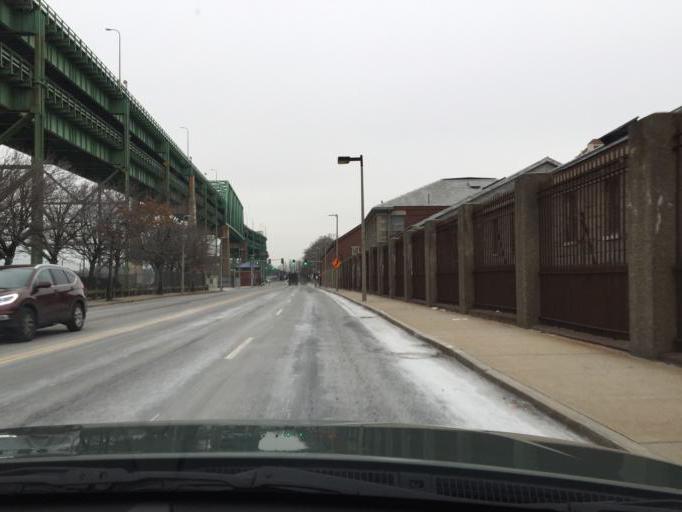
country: US
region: Massachusetts
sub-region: Suffolk County
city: Boston
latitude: 42.3776
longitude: -71.0537
